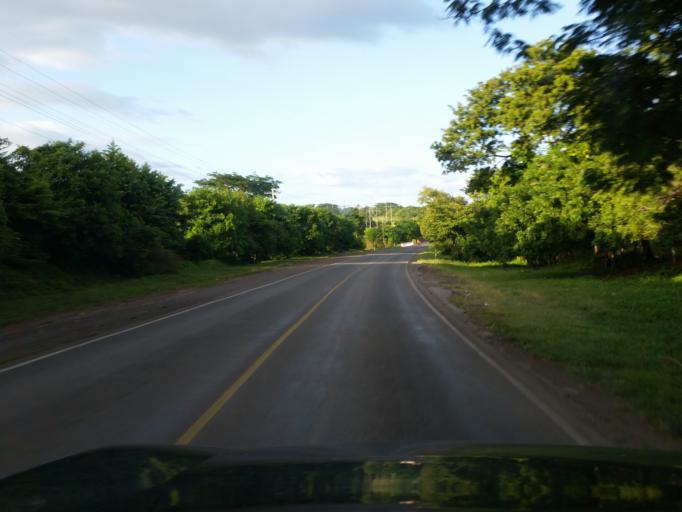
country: NI
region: Granada
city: Nandaime
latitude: 11.7917
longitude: -86.0491
